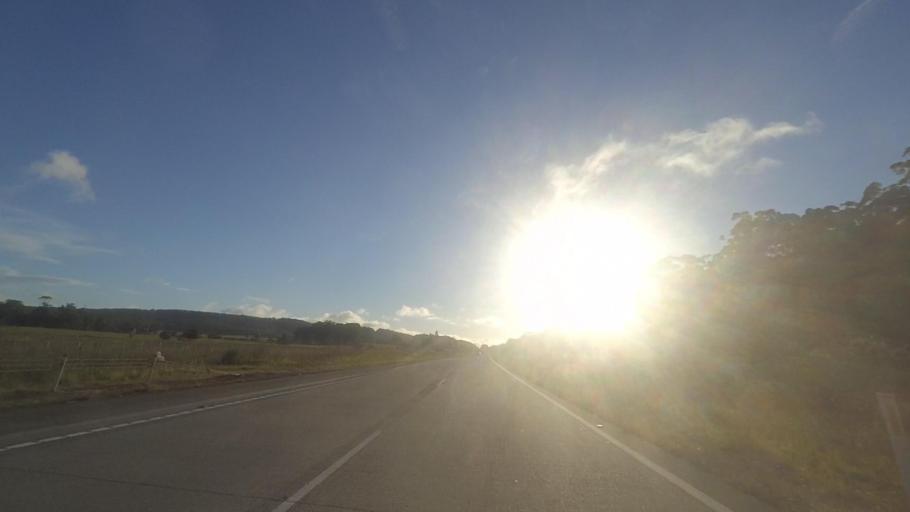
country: AU
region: New South Wales
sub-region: Great Lakes
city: Bulahdelah
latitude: -32.5223
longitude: 152.2012
